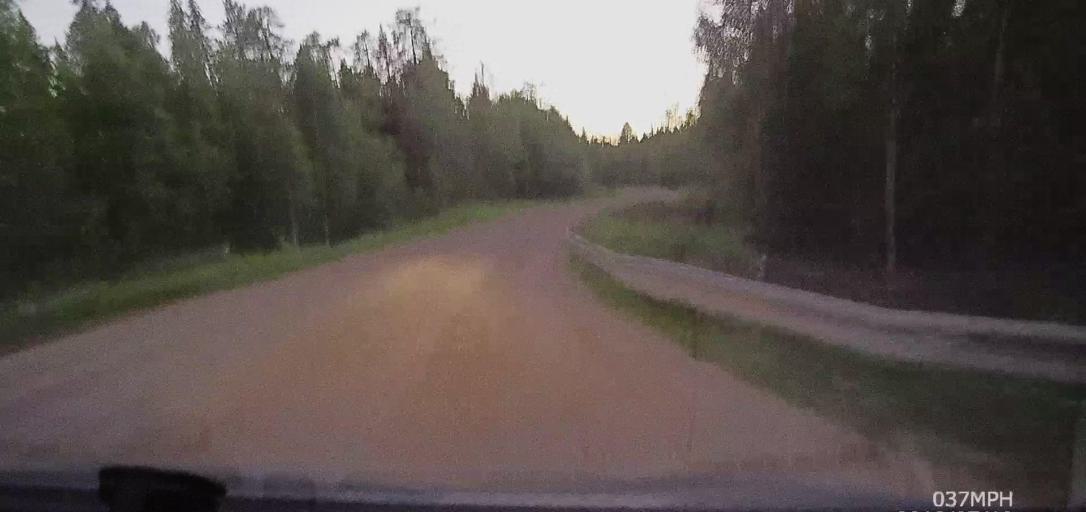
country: RU
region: Arkhangelskaya
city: Pinega
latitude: 64.4226
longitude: 43.1407
